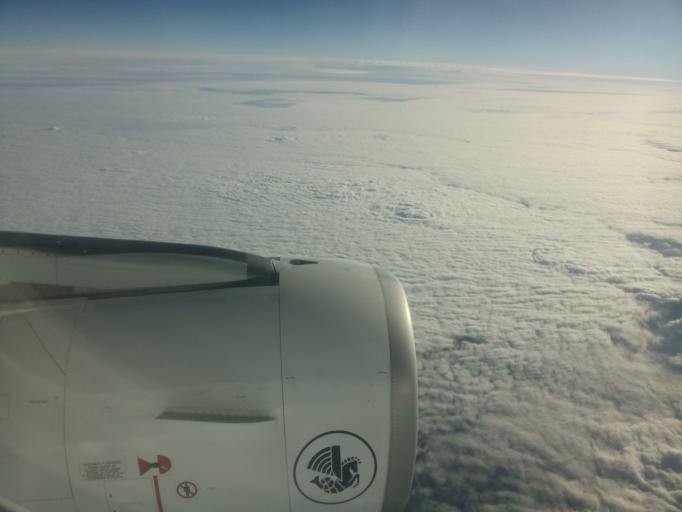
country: DE
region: Rheinland-Pfalz
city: Kenn
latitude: 49.8116
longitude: 6.6741
